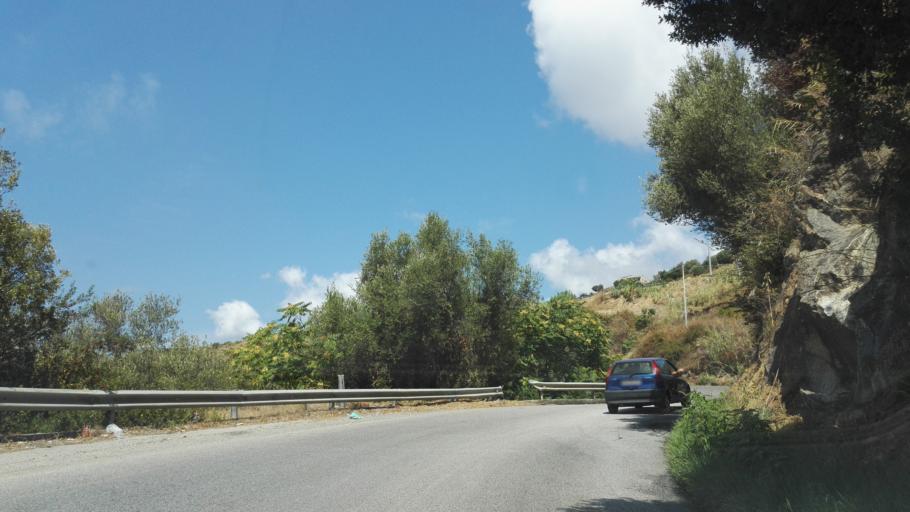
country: IT
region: Calabria
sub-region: Provincia di Vibo-Valentia
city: Nicotera
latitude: 38.5538
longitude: 15.9285
